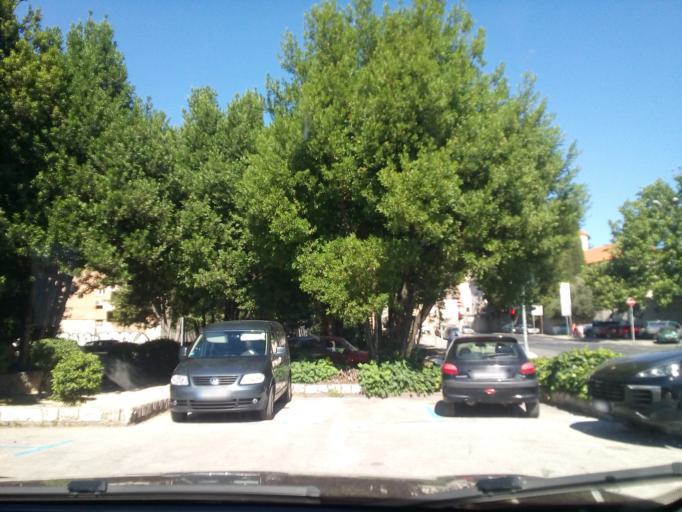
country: HR
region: Splitsko-Dalmatinska
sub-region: Grad Split
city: Split
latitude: 43.5050
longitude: 16.4484
